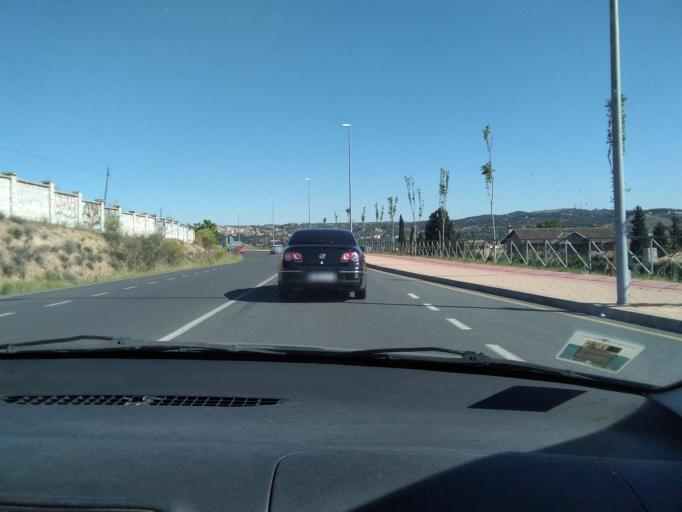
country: ES
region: Castille-La Mancha
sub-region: Province of Toledo
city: Toledo
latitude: 39.8824
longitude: -4.0525
